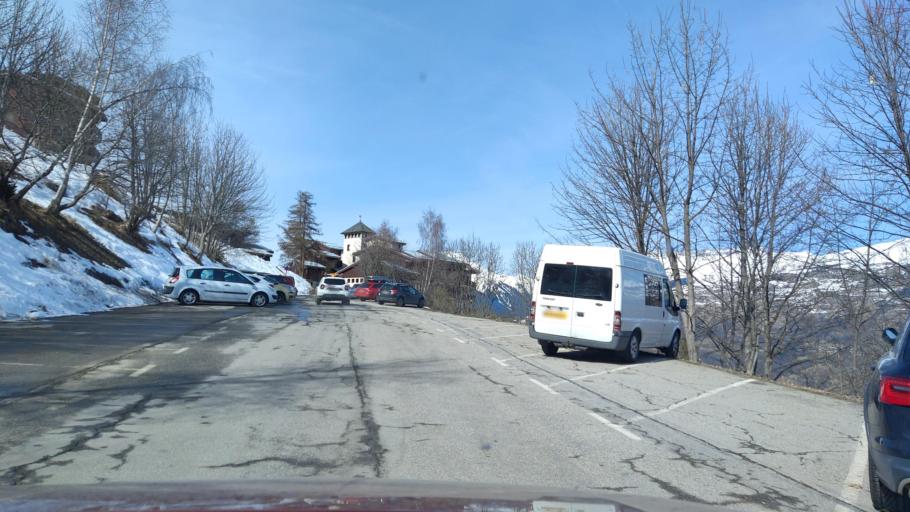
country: FR
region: Rhone-Alpes
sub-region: Departement de la Savoie
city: Belle-Plagne
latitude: 45.5593
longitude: 6.7397
